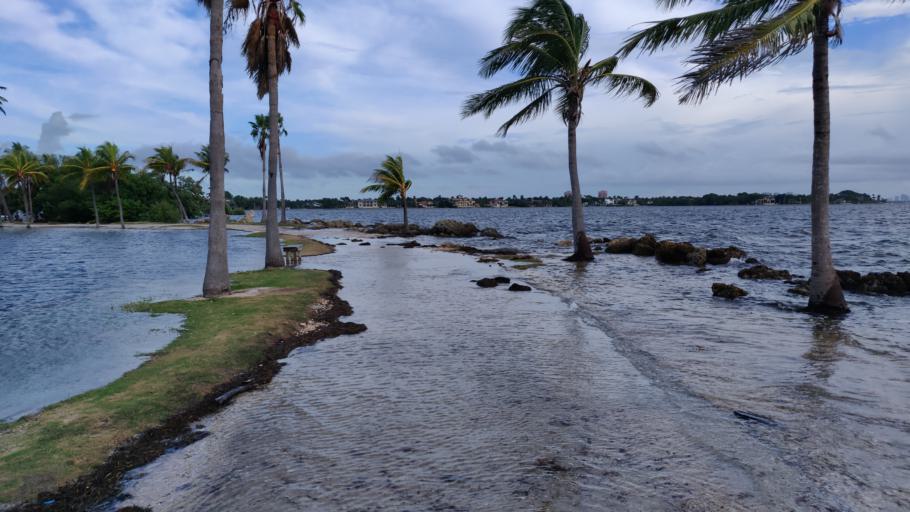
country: US
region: Florida
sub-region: Miami-Dade County
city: Coconut Grove
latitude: 25.6785
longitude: -80.2555
